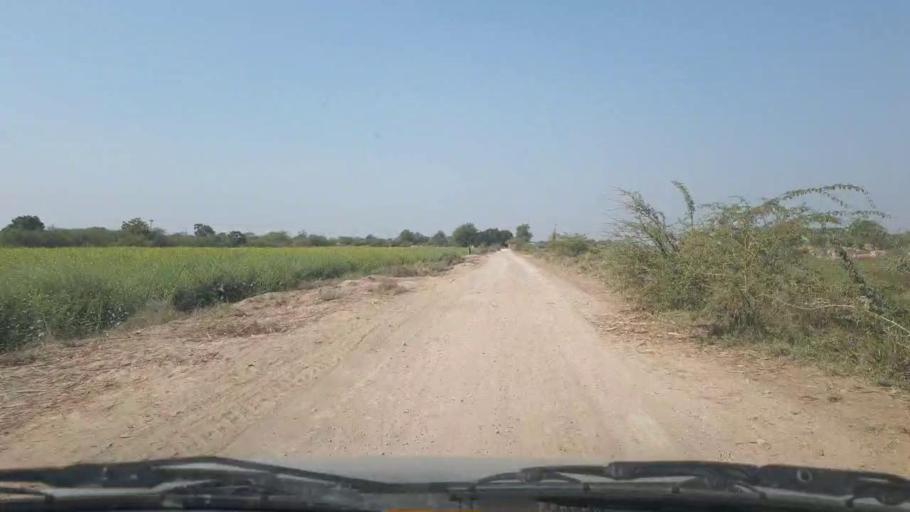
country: PK
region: Sindh
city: Samaro
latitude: 25.2252
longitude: 69.3262
